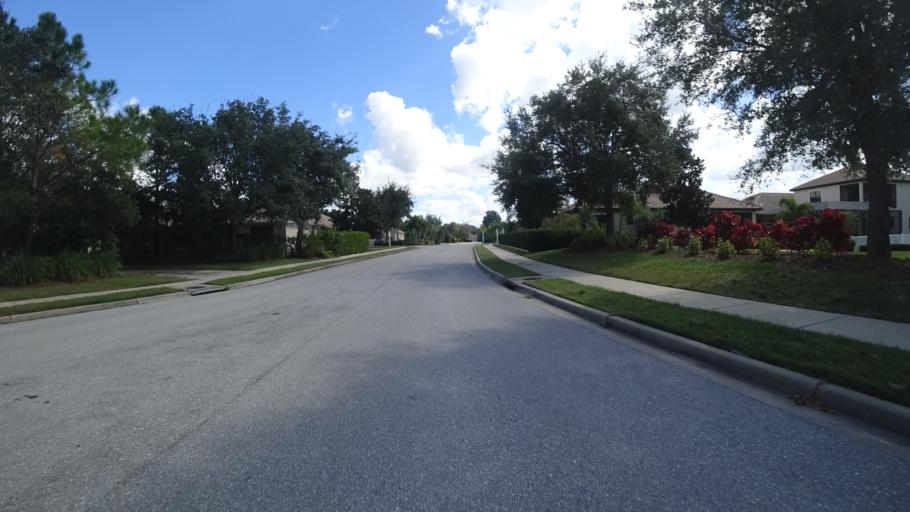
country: US
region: Florida
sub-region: Sarasota County
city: The Meadows
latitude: 27.4237
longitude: -82.3914
